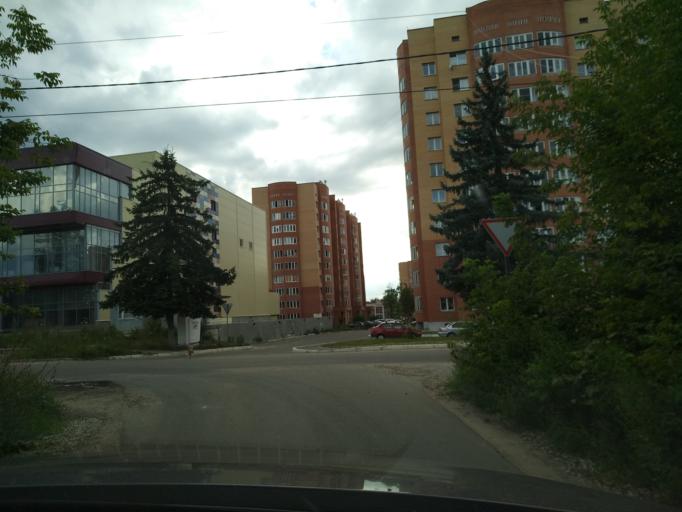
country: RU
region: Moskovskaya
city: Yegor'yevsk
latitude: 55.3680
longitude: 39.0809
